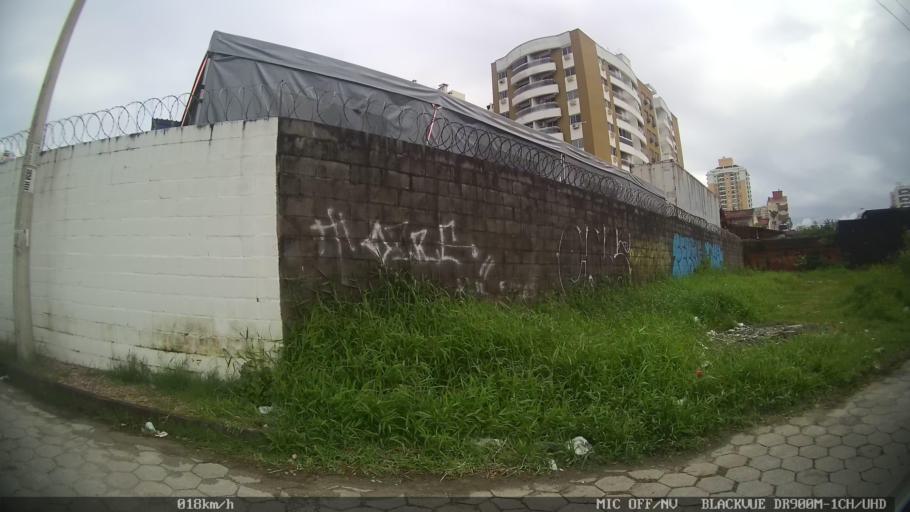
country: BR
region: Santa Catarina
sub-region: Sao Jose
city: Campinas
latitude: -27.5792
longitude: -48.6023
